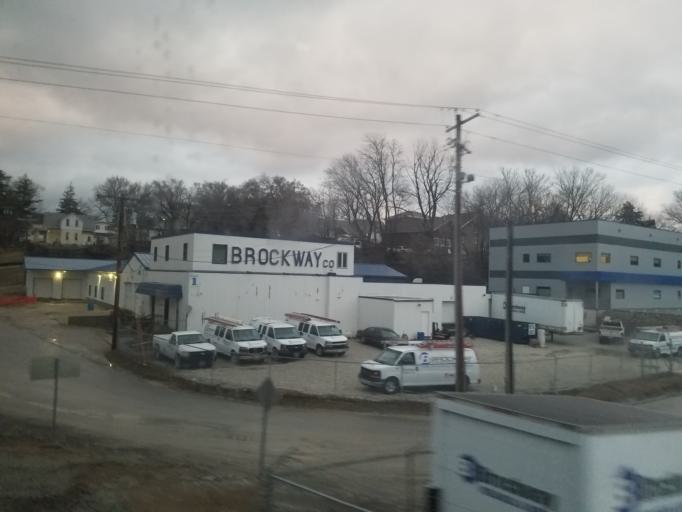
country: US
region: Iowa
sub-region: Des Moines County
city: Burlington
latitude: 40.8193
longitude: -91.1121
